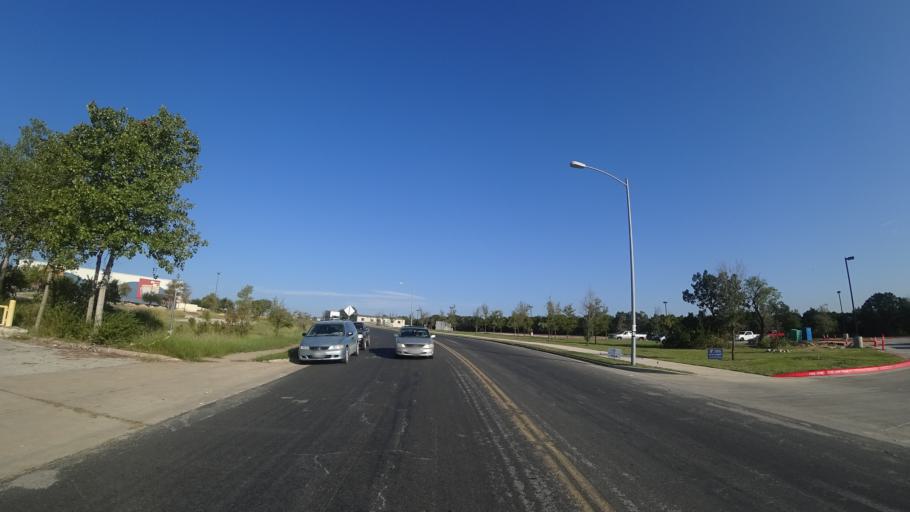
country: US
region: Texas
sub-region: Travis County
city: Austin
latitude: 30.3169
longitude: -97.6584
